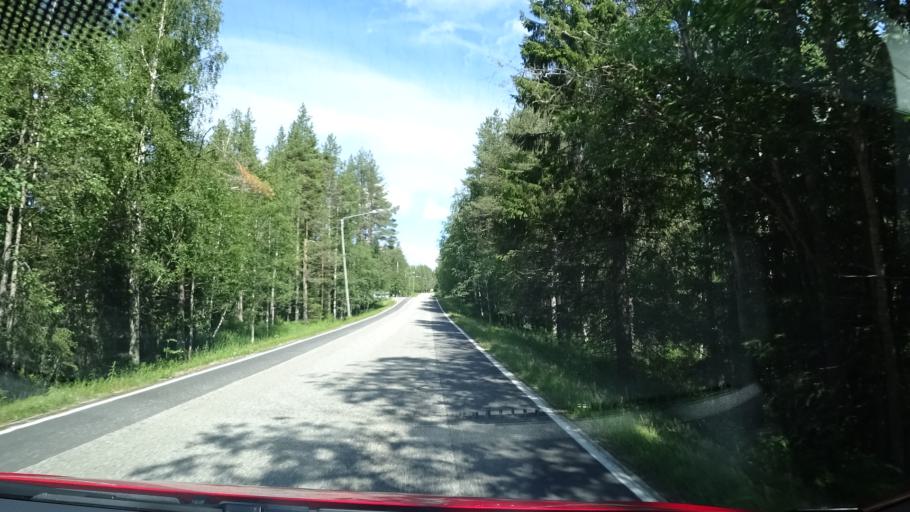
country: FI
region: Kainuu
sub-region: Kehys-Kainuu
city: Kuhmo
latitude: 64.6721
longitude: 29.6708
